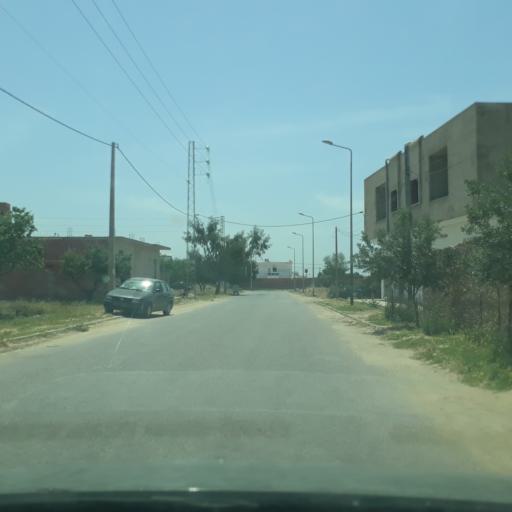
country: TN
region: Safaqis
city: Al Qarmadah
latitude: 34.8248
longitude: 10.7857
